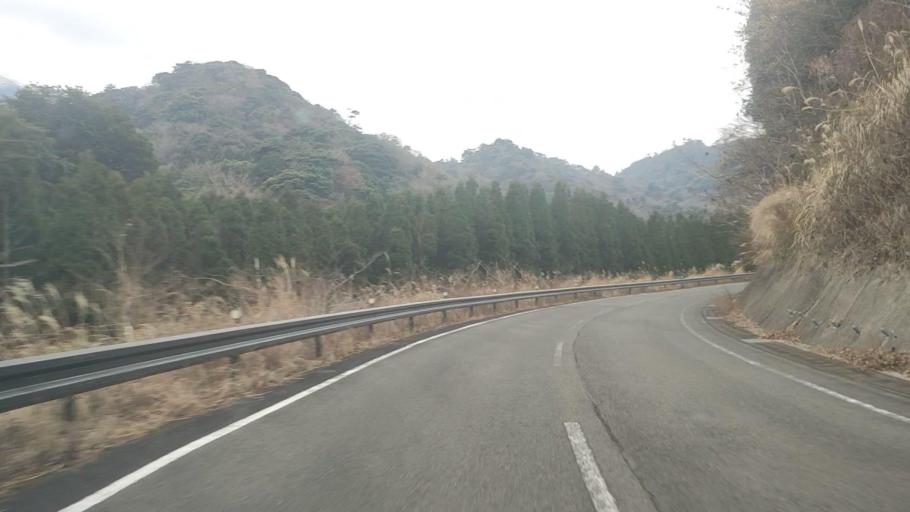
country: JP
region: Nagasaki
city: Shimabara
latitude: 32.7838
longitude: 130.2821
